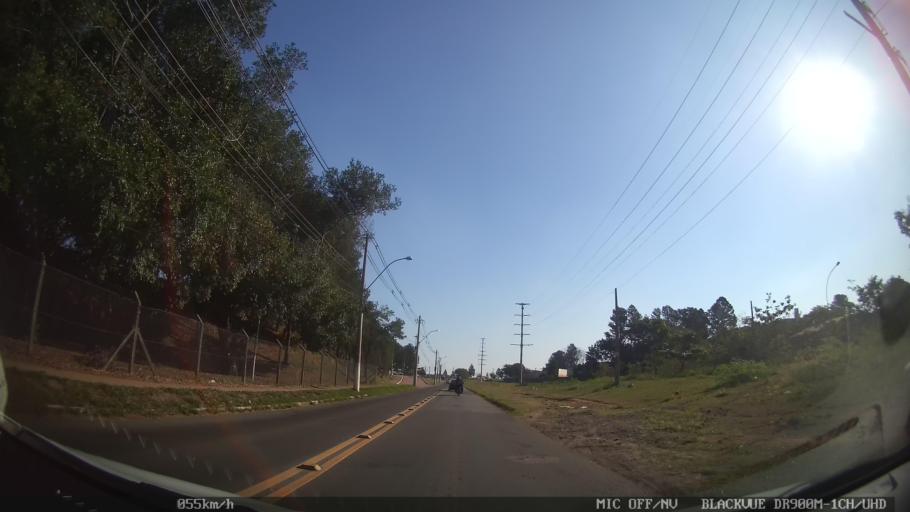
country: BR
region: Sao Paulo
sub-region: Campinas
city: Campinas
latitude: -22.9960
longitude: -47.1283
